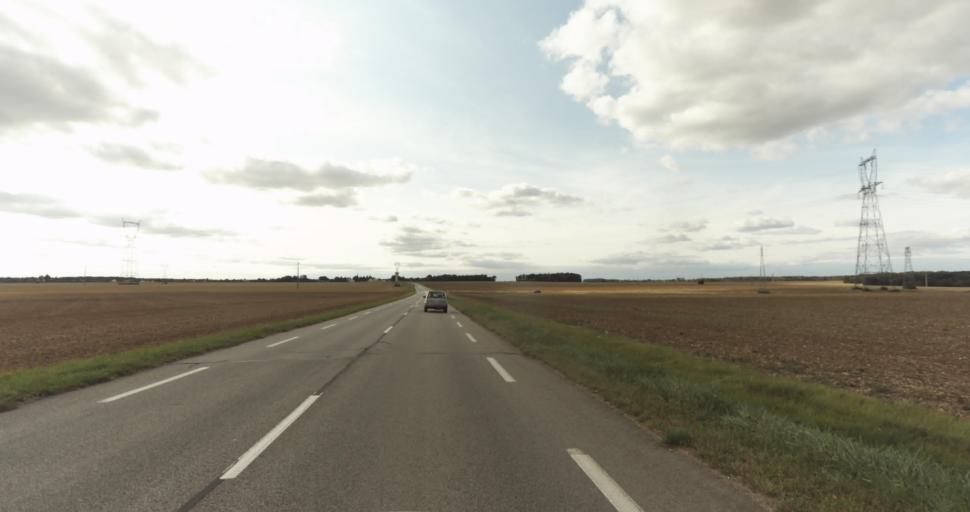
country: FR
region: Haute-Normandie
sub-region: Departement de l'Eure
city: La Couture-Boussey
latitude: 48.8928
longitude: 1.4261
